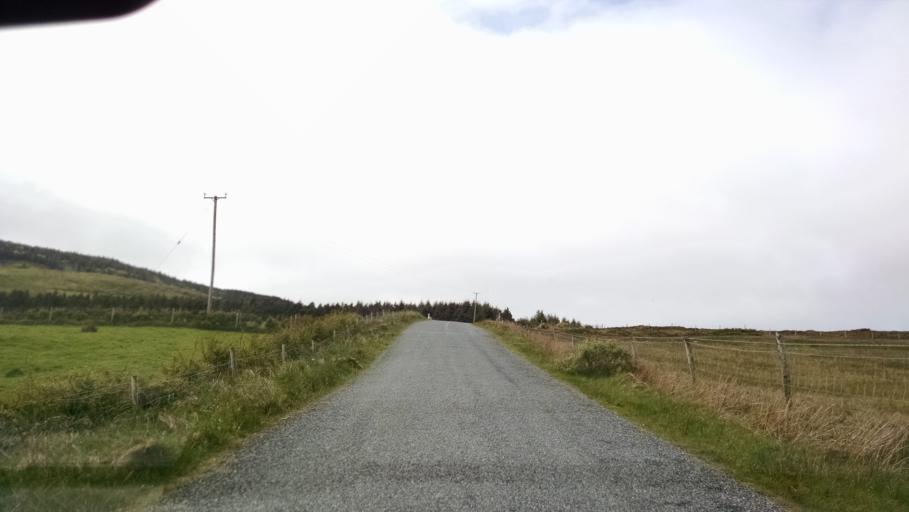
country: IE
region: Connaught
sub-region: County Galway
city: Clifden
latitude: 53.7079
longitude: -9.8340
